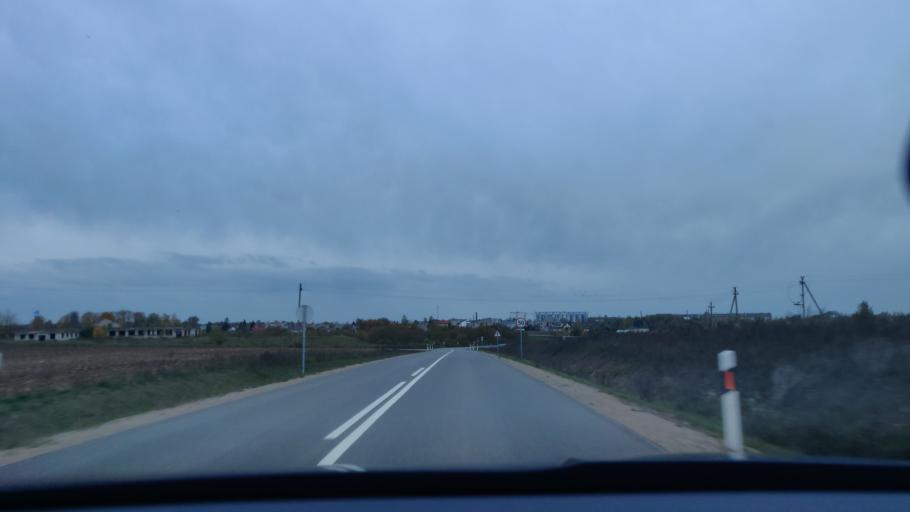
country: LT
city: Trakai
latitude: 54.6068
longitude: 24.9963
